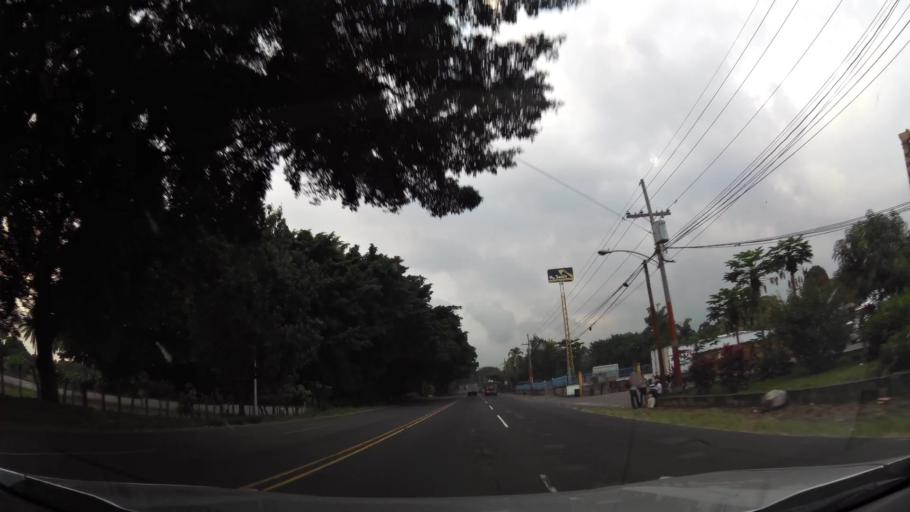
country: GT
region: Escuintla
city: Siquinala
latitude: 14.2898
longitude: -90.9398
